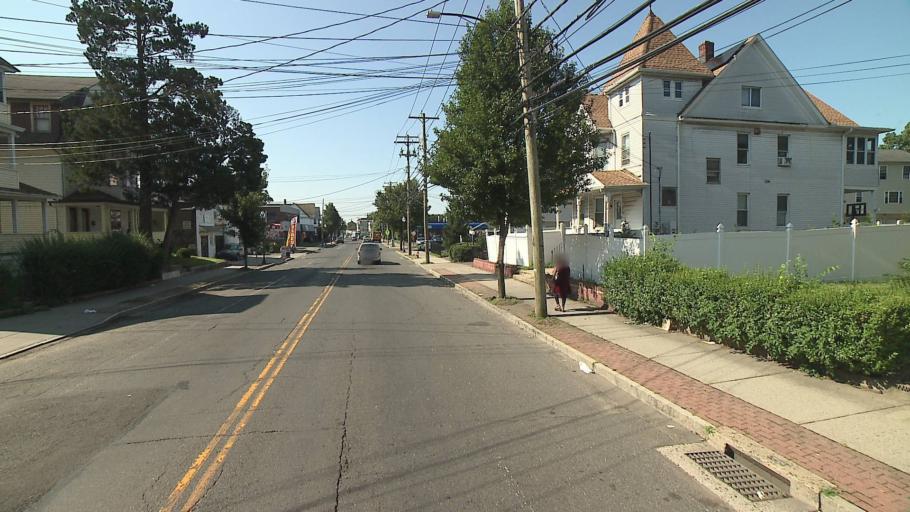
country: US
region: Connecticut
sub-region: Fairfield County
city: Bridgeport
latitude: 41.2010
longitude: -73.1799
